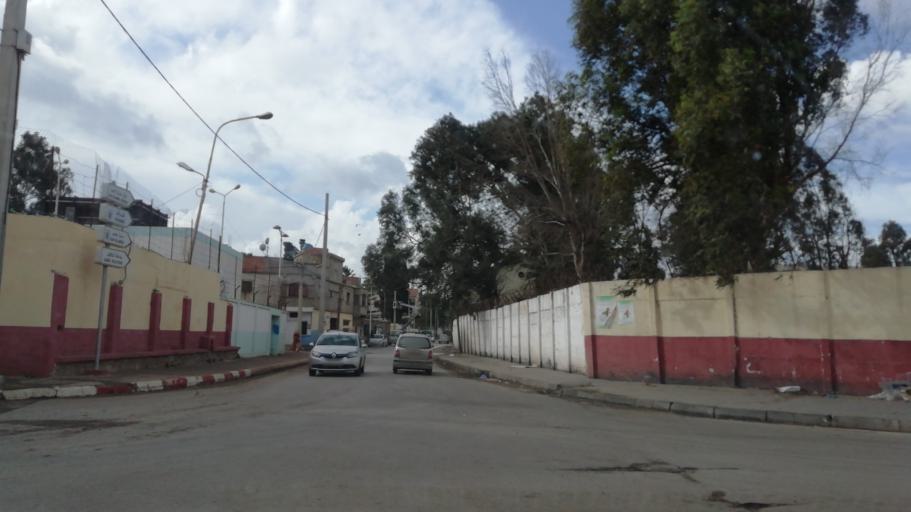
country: DZ
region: Oran
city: Oran
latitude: 35.6777
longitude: -0.6205
